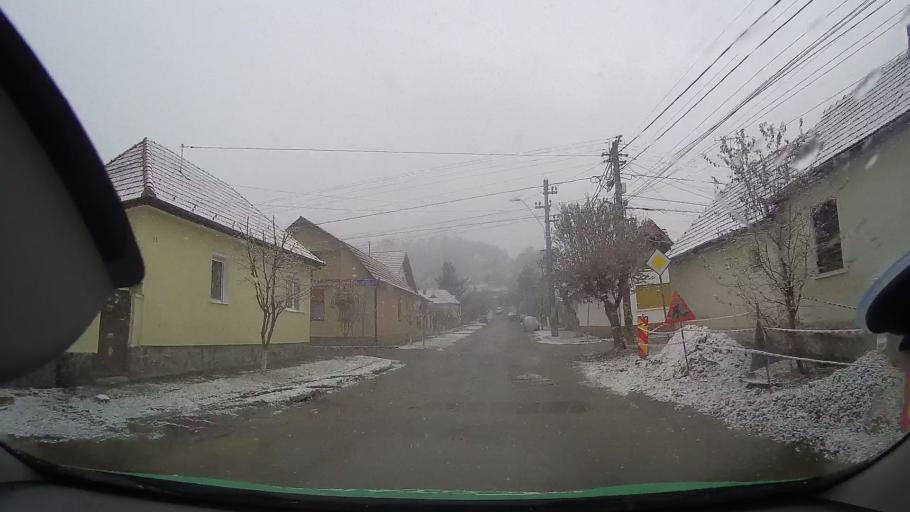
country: RO
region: Sibiu
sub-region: Municipiul Medias
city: Medias
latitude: 46.1629
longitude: 24.3637
